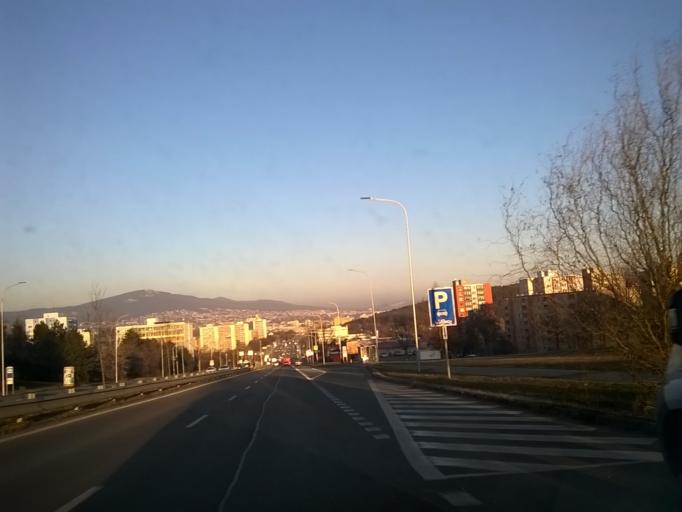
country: SK
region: Nitriansky
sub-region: Okres Nitra
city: Nitra
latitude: 48.2993
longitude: 18.0576
